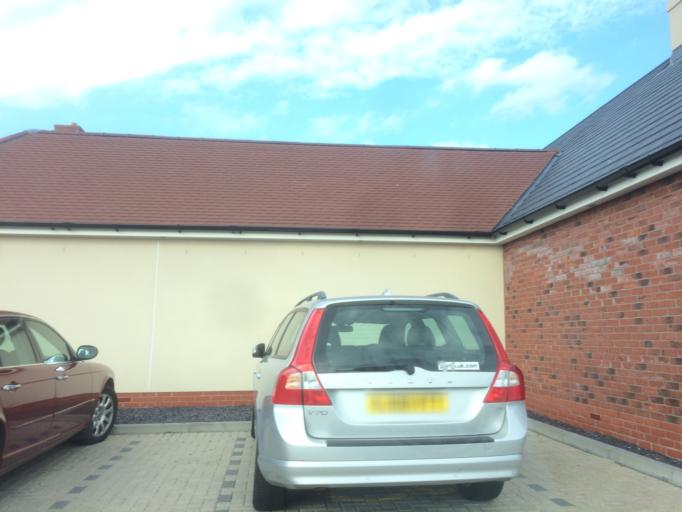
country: GB
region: Scotland
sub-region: East Renfrewshire
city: Newton Mearns
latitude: 55.8018
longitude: -4.3423
